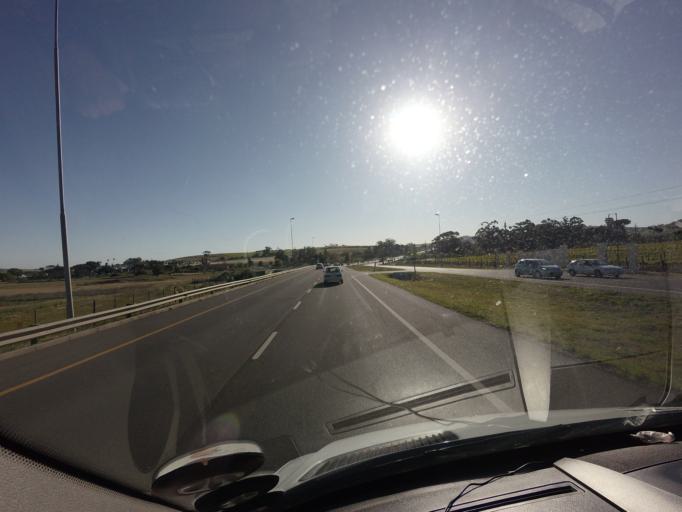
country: ZA
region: Western Cape
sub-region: Cape Winelands District Municipality
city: Stellenbosch
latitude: -33.9527
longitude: 18.8016
